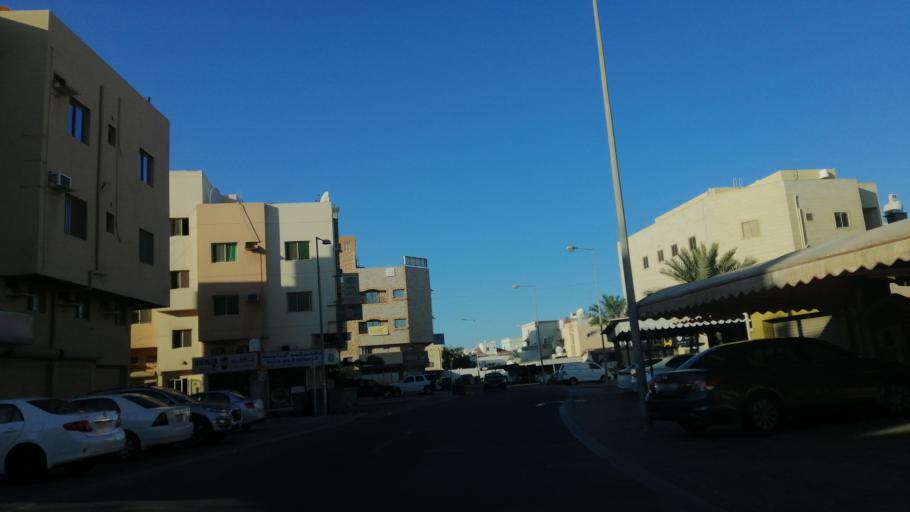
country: BH
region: Muharraq
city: Al Hadd
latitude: 26.2460
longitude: 50.6558
